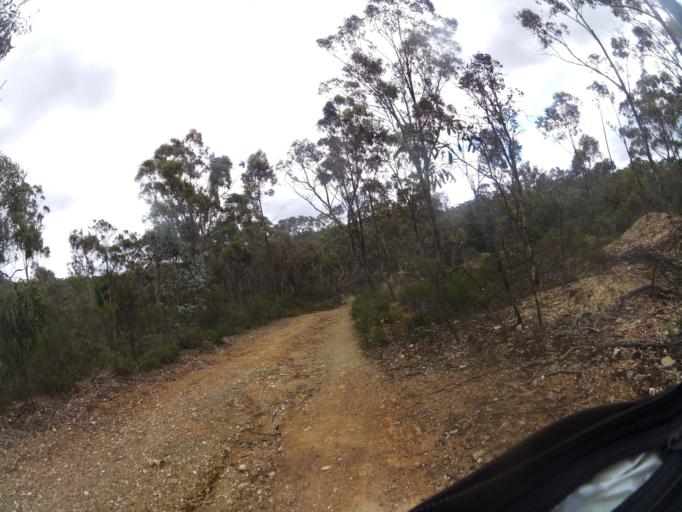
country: AU
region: Victoria
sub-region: Mount Alexander
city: Castlemaine
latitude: -37.0728
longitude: 144.2547
